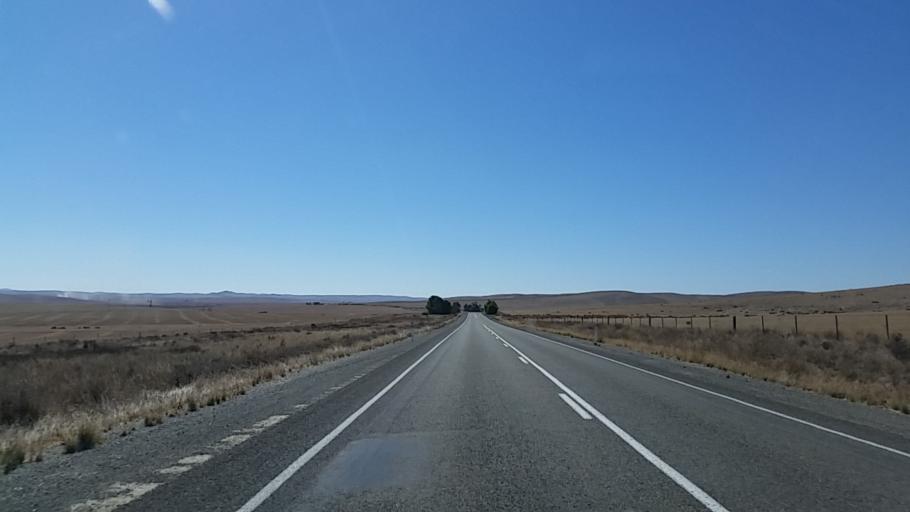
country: AU
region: South Australia
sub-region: Northern Areas
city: Jamestown
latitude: -33.3205
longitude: 138.8836
